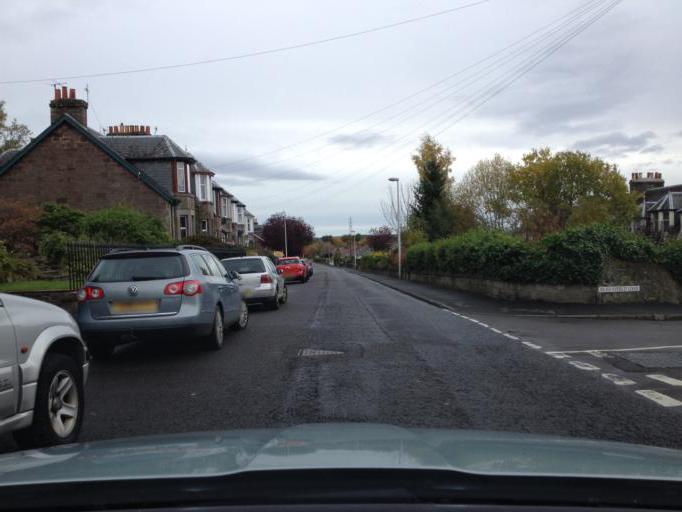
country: GB
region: Scotland
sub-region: Perth and Kinross
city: Crieff
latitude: 56.3736
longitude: -3.8320
